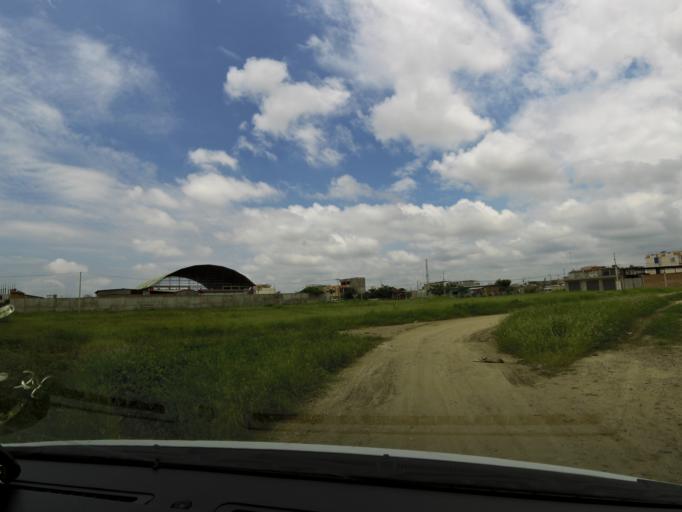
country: EC
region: El Oro
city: Huaquillas
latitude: -3.4856
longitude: -80.2185
